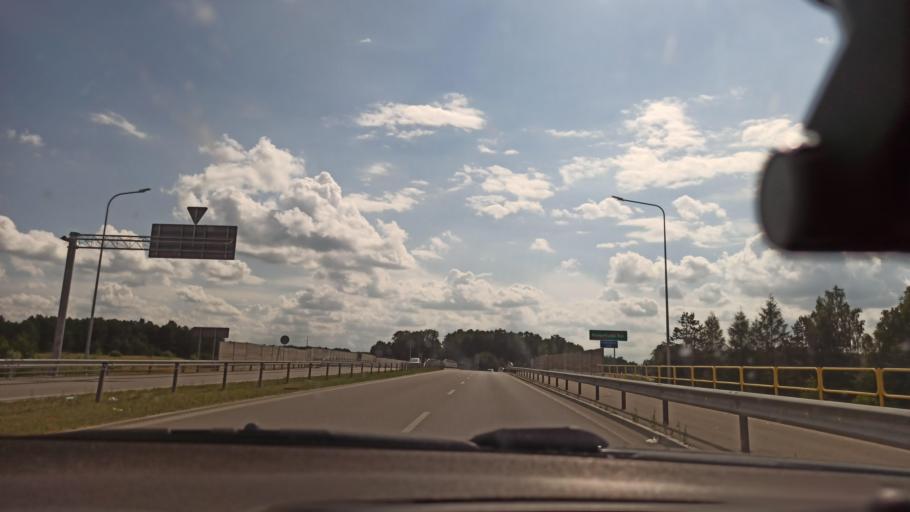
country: PL
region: Podlasie
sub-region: Powiat bialostocki
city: Turosn Koscielna
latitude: 53.0681
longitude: 23.0773
